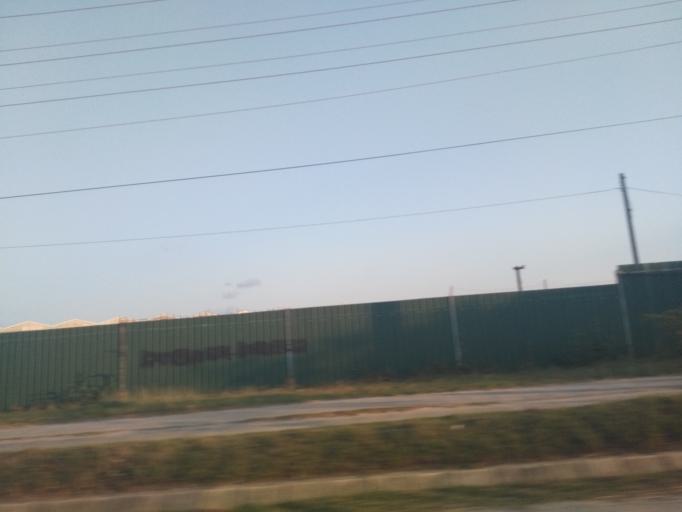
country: TZ
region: Dar es Salaam
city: Dar es Salaam
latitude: -6.8608
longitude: 39.2114
